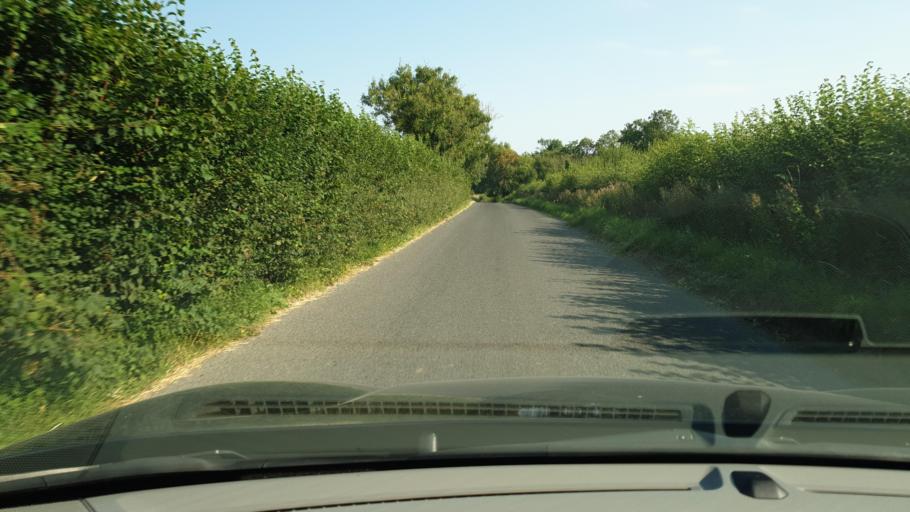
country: IE
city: Kentstown
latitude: 53.6018
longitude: -6.4950
